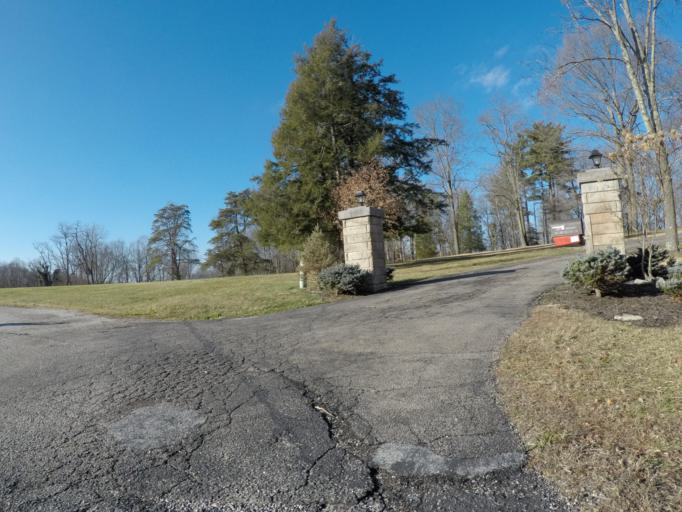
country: US
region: West Virginia
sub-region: Cabell County
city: Pea Ridge
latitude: 38.4002
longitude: -82.3269
